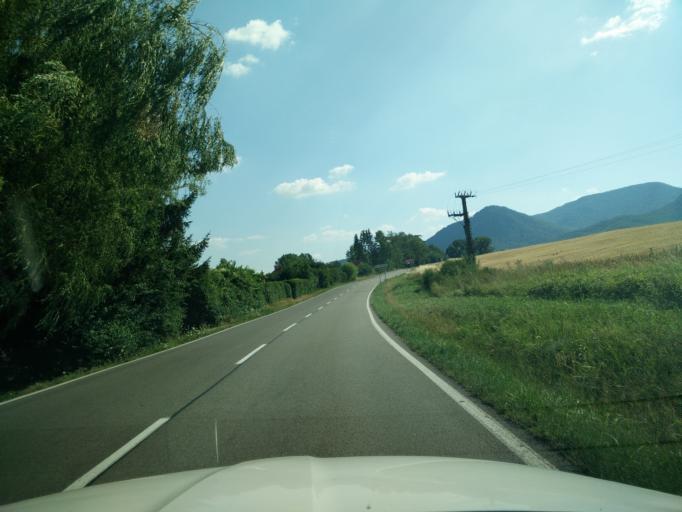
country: SK
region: Nitriansky
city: Bojnice
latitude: 48.8117
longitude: 18.4768
